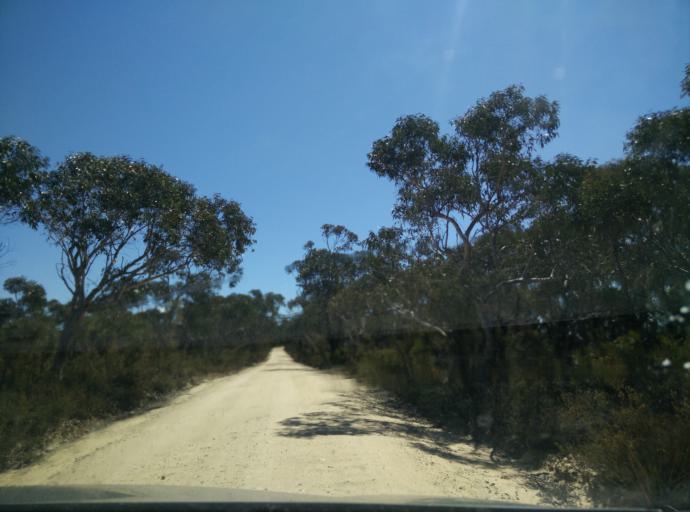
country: AU
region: New South Wales
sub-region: Blue Mountains Municipality
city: Blackheath
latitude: -33.5766
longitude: 150.2773
